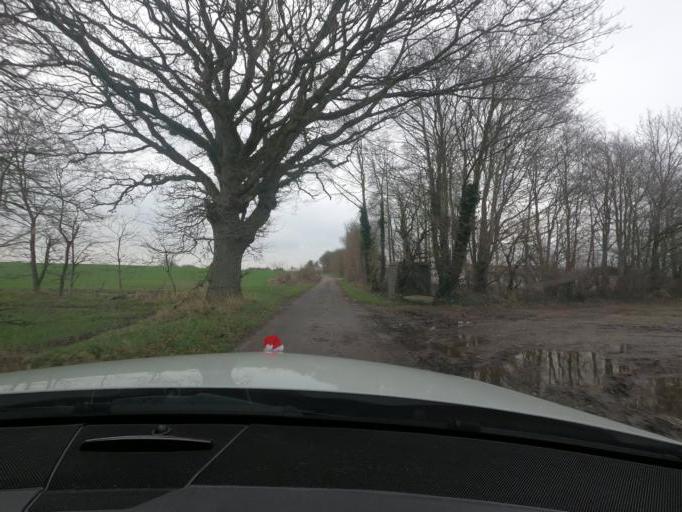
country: DK
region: South Denmark
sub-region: Haderslev Kommune
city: Starup
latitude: 55.2401
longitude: 9.7090
